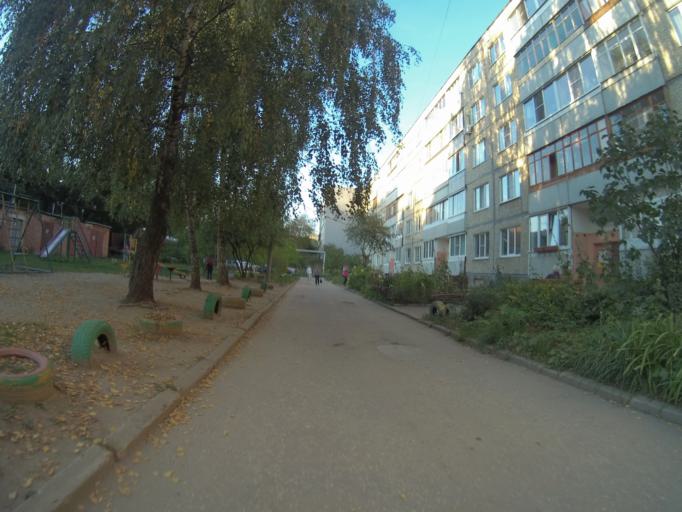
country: RU
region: Vladimir
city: Vladimir
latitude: 56.1127
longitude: 40.3781
